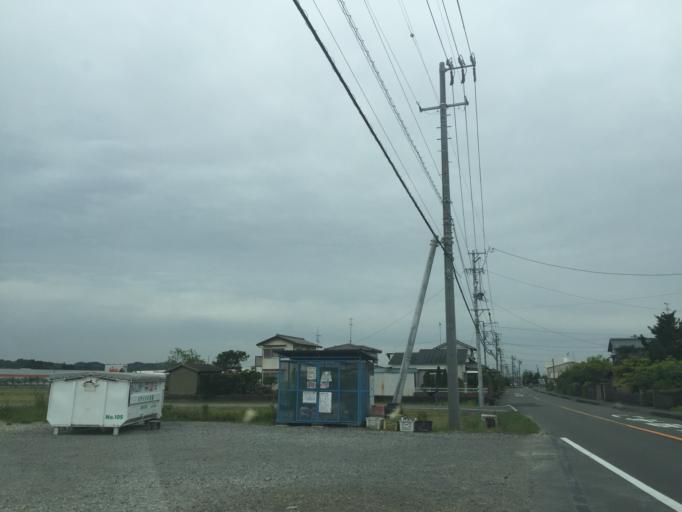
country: JP
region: Shizuoka
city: Kakegawa
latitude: 34.7644
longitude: 137.9796
